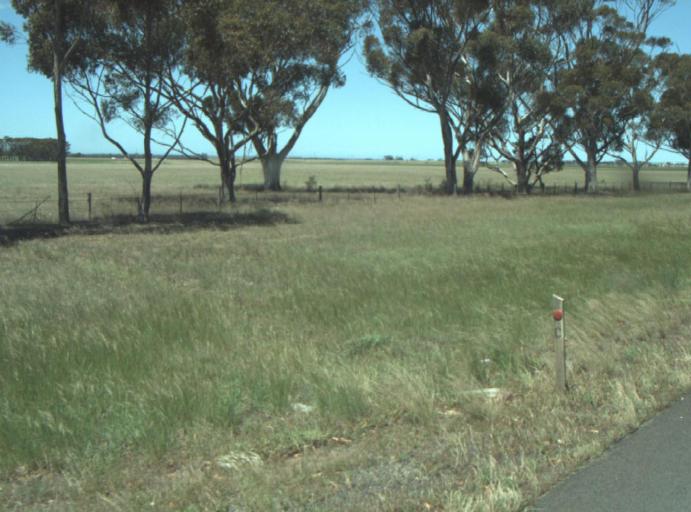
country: AU
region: Victoria
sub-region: Greater Geelong
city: Lara
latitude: -37.9488
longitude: 144.3546
